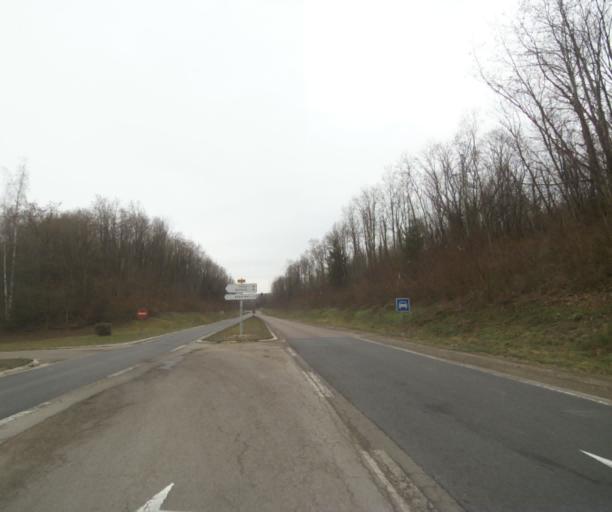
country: FR
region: Champagne-Ardenne
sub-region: Departement de la Haute-Marne
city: Bienville
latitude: 48.5711
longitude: 5.0351
